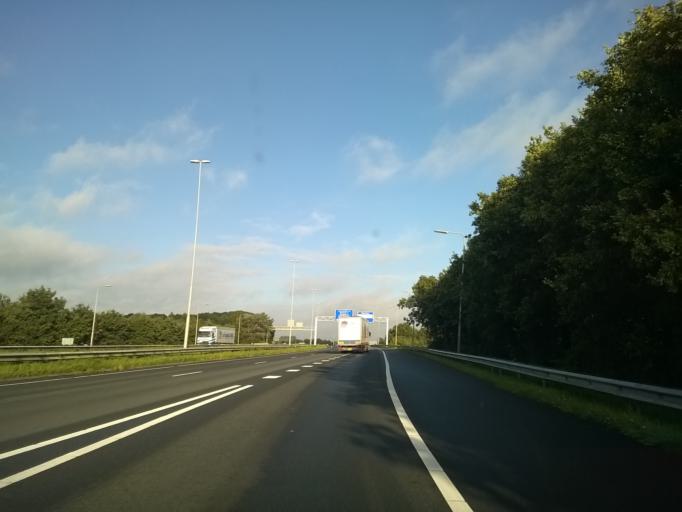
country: NL
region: Friesland
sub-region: Gemeente Smallingerland
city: Drachtstercompagnie
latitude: 53.1070
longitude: 6.1327
